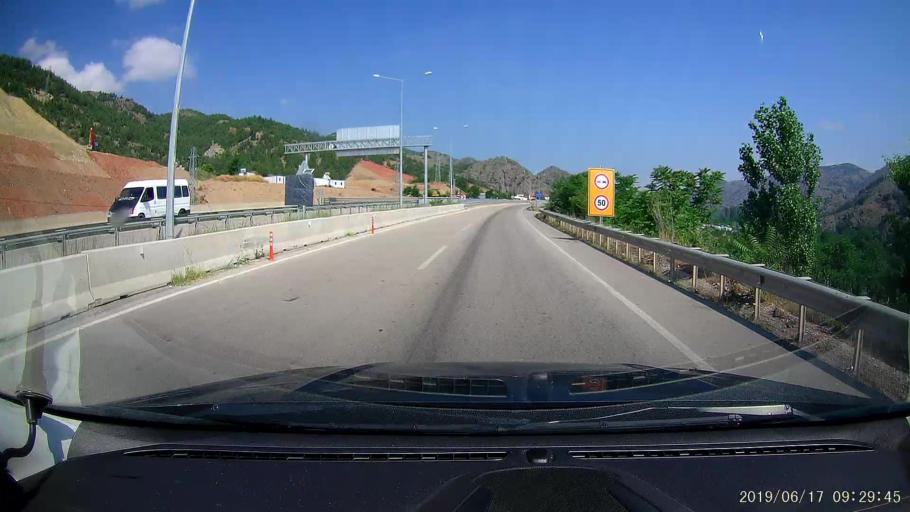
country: TR
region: Amasya
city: Amasya
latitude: 40.6987
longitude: 35.8084
